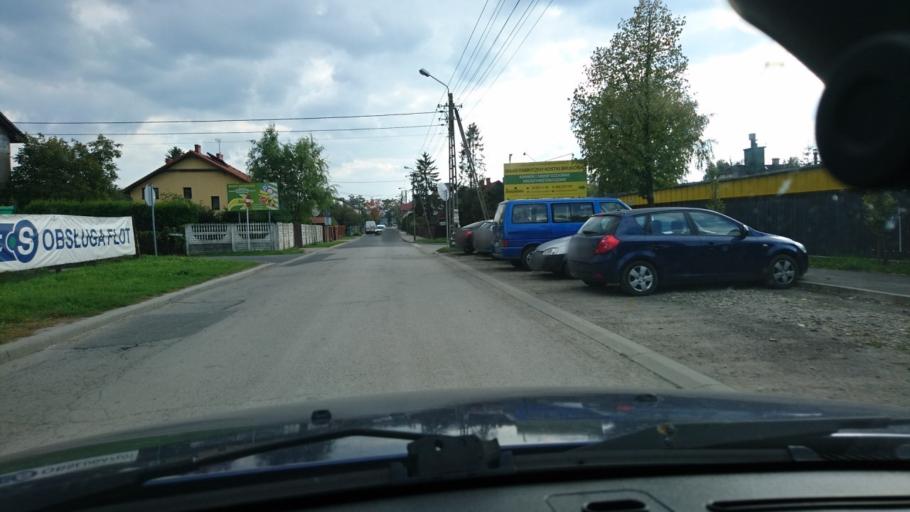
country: PL
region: Silesian Voivodeship
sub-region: Bielsko-Biala
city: Bielsko-Biala
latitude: 49.8431
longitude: 19.0557
